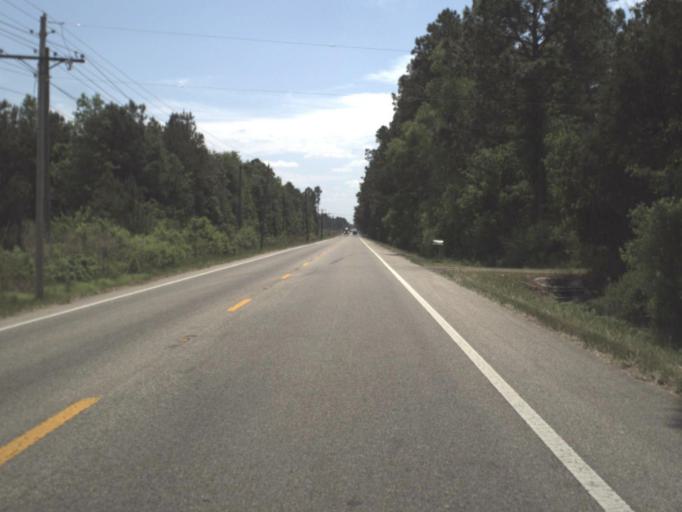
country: US
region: Florida
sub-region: Calhoun County
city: Blountstown
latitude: 30.5241
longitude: -85.1296
